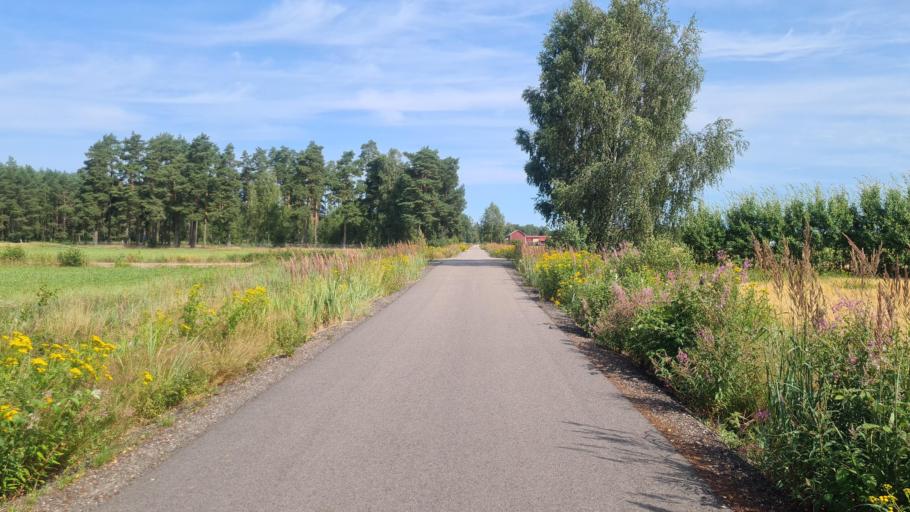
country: SE
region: Kronoberg
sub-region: Ljungby Kommun
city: Lagan
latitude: 56.8995
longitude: 13.9891
